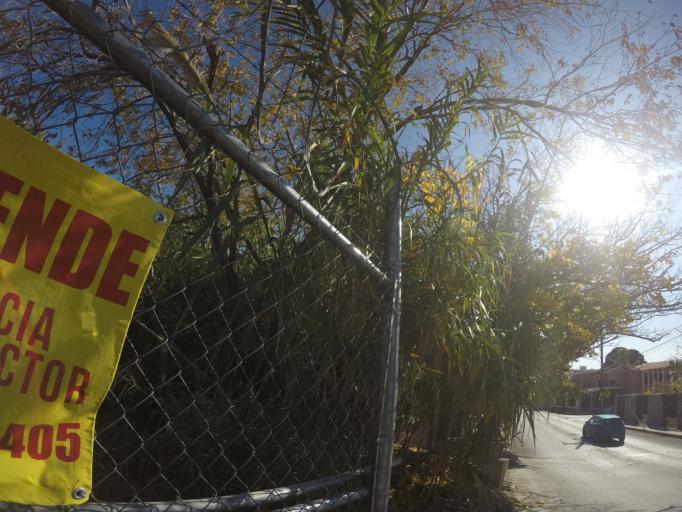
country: MX
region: Chihuahua
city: Ciudad Juarez
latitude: 31.7271
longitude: -106.4133
